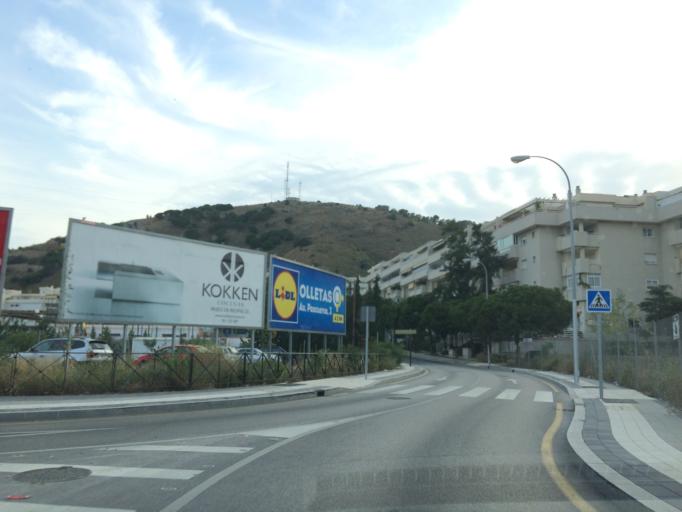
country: ES
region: Andalusia
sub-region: Provincia de Malaga
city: Malaga
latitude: 36.7338
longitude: -4.4006
